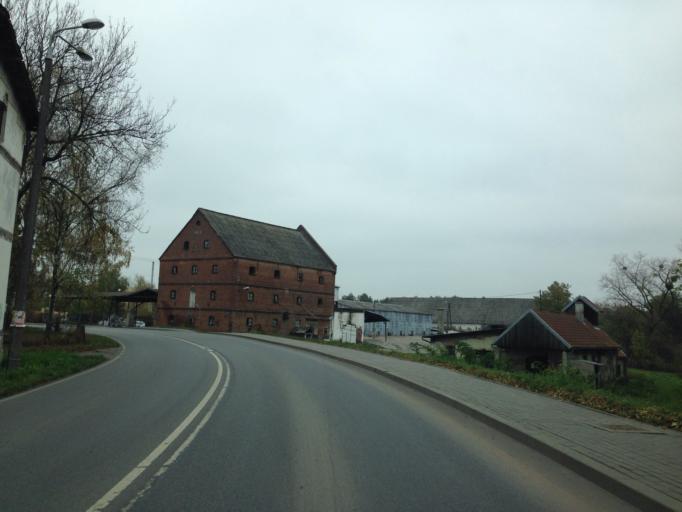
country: PL
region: Kujawsko-Pomorskie
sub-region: Powiat grudziadzki
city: Radzyn Chelminski
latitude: 53.3897
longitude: 18.9367
